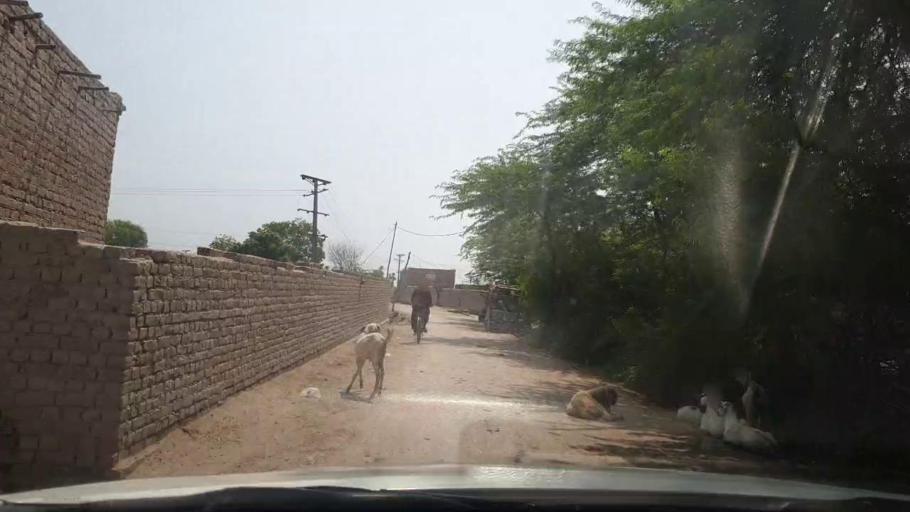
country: PK
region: Sindh
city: Shikarpur
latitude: 27.9878
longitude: 68.7147
